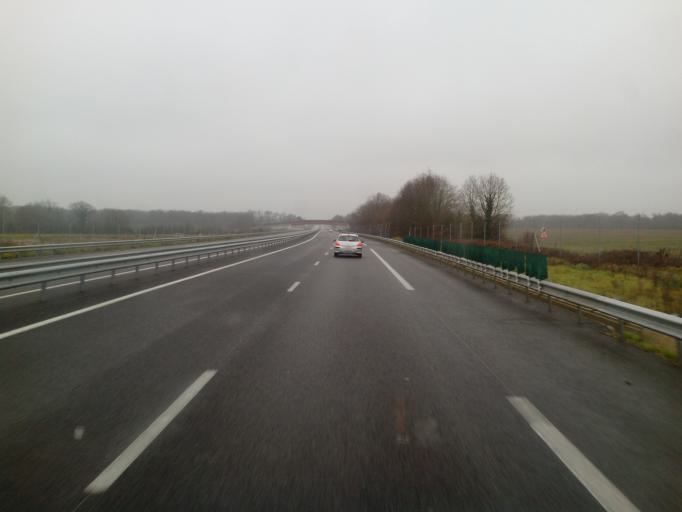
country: FR
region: Poitou-Charentes
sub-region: Departement de la Vienne
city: Savigny-Levescault
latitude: 46.4921
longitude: 0.4976
